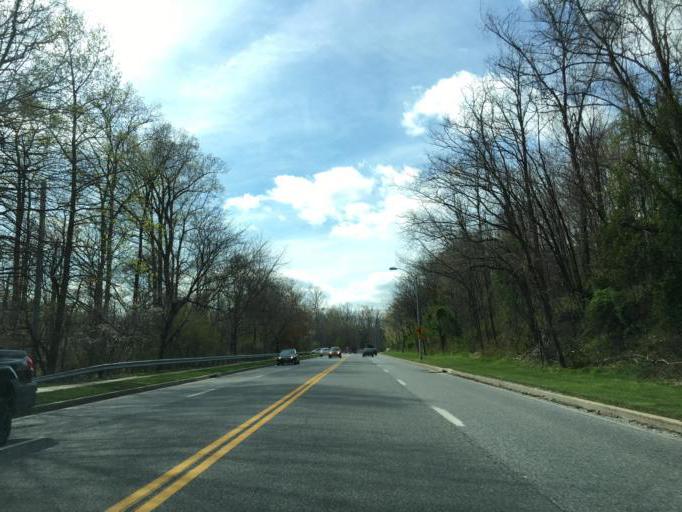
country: US
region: Maryland
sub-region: Baltimore County
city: Mays Chapel
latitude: 39.4532
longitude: -76.6554
